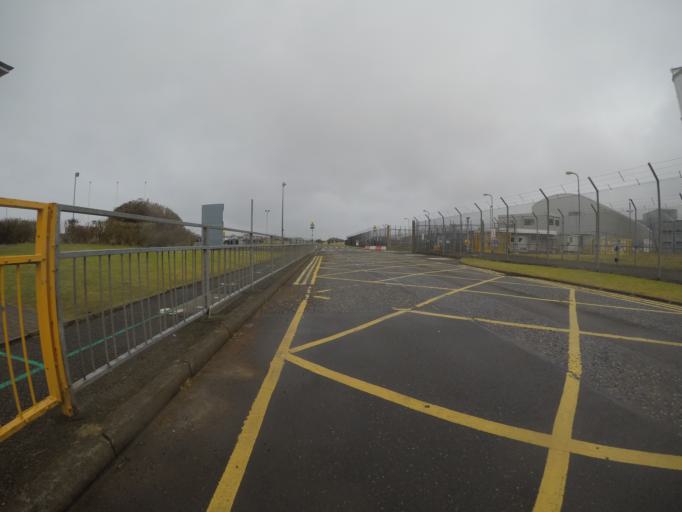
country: GB
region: Scotland
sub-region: North Ayrshire
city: Millport
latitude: 55.7198
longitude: -4.8998
